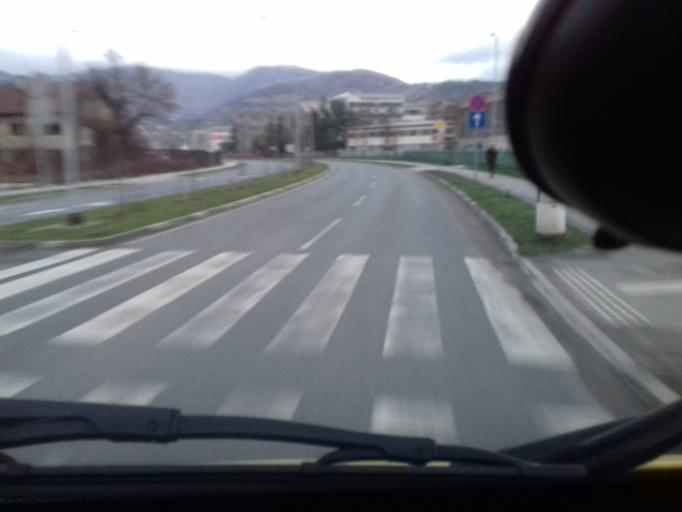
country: BA
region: Federation of Bosnia and Herzegovina
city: Zenica
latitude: 44.2100
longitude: 17.9065
